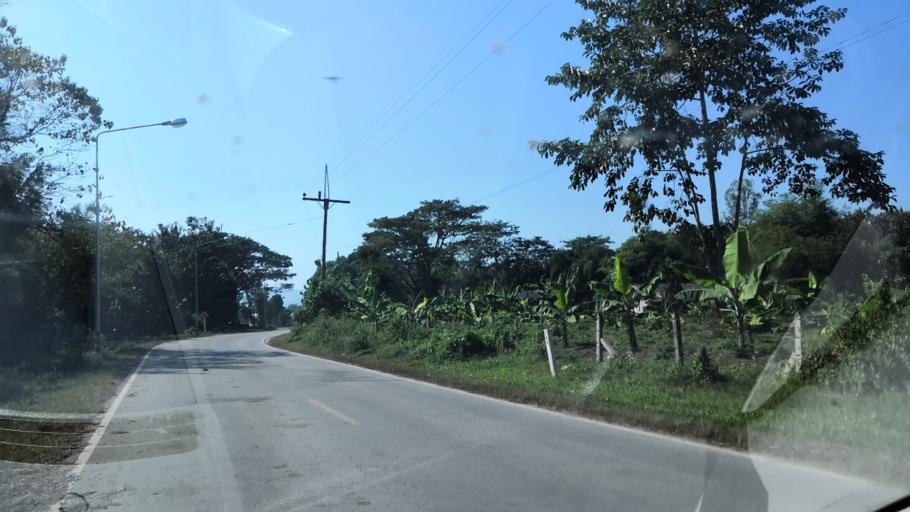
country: TH
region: Chiang Rai
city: Wiang Chai
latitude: 19.8493
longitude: 99.9360
